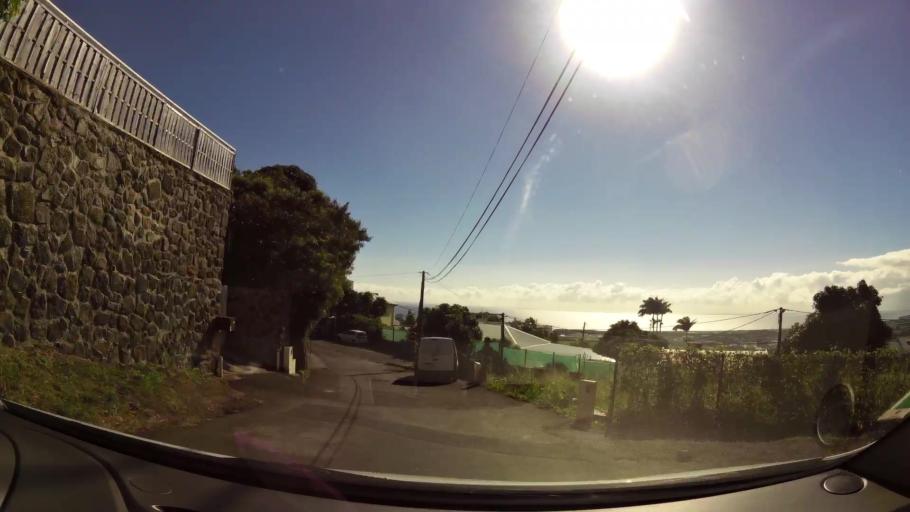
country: RE
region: Reunion
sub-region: Reunion
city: Saint-Denis
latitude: -20.9123
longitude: 55.4822
